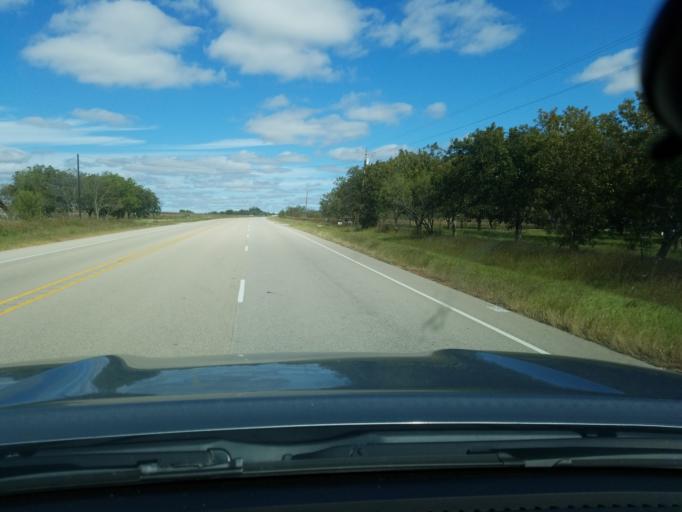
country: US
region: Texas
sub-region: Hamilton County
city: Hamilton
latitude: 31.6451
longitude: -98.1481
